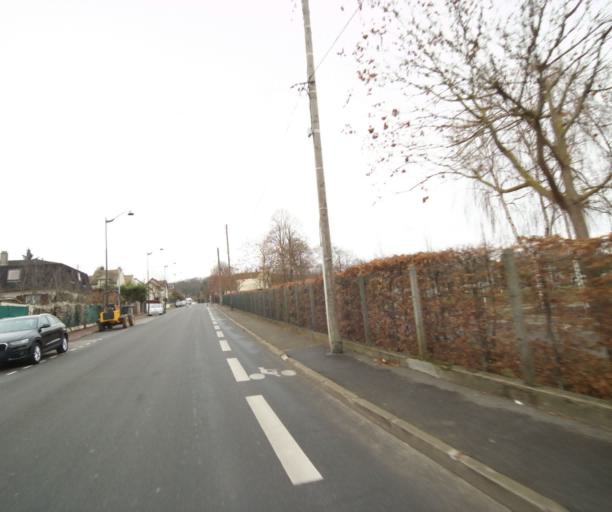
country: FR
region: Ile-de-France
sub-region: Departement des Hauts-de-Seine
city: Rueil-Malmaison
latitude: 48.8636
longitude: 2.1788
